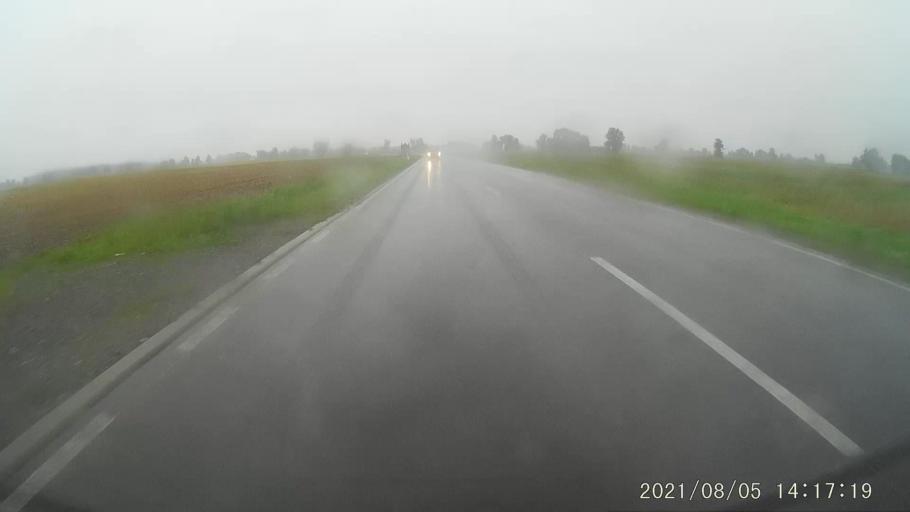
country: PL
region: Opole Voivodeship
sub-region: Powiat prudnicki
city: Biala
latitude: 50.4603
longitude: 17.7074
